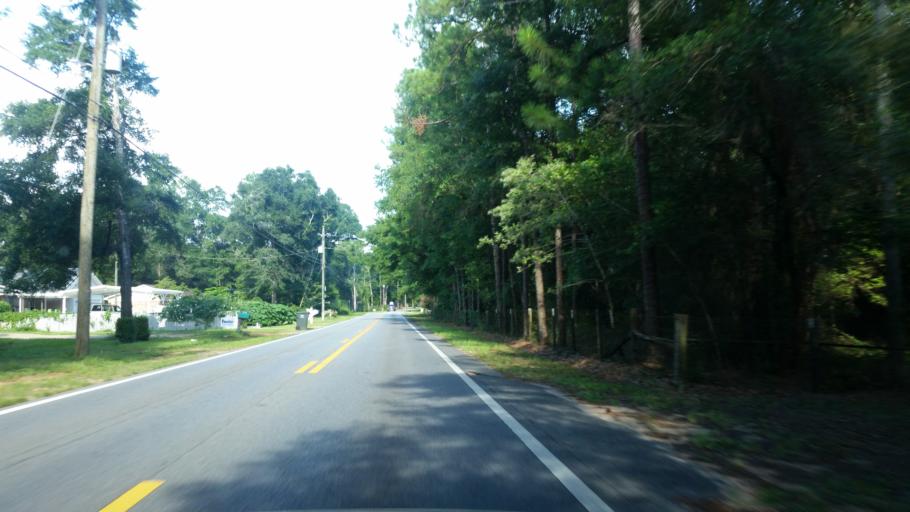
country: US
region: Florida
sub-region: Santa Rosa County
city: Milton
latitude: 30.6215
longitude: -87.0803
